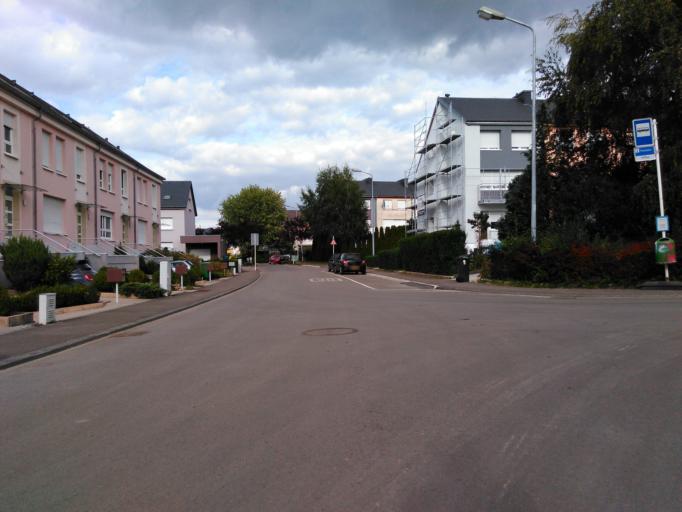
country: LU
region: Luxembourg
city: Belvaux
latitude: 49.5184
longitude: 5.9142
